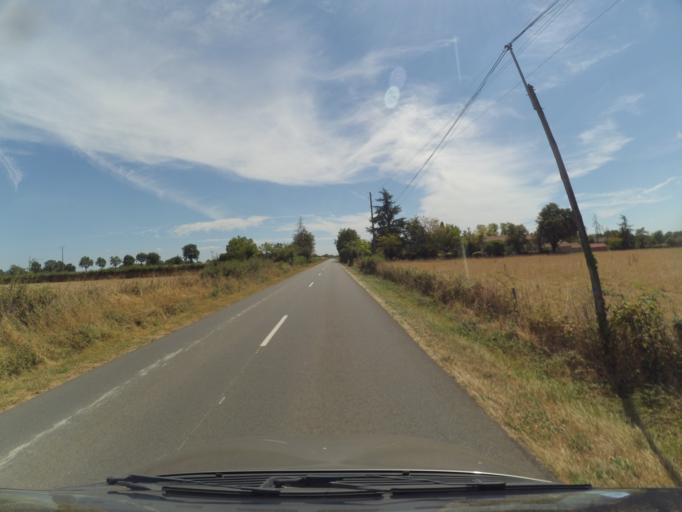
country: FR
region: Poitou-Charentes
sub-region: Departement de la Vienne
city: Availles-Limouzine
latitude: 46.1522
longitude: 0.5531
